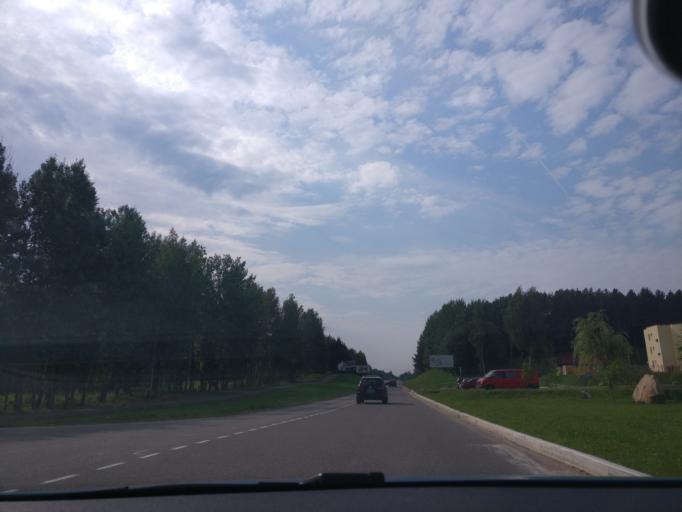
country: BY
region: Minsk
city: Lahoysk
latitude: 54.1913
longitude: 27.8307
